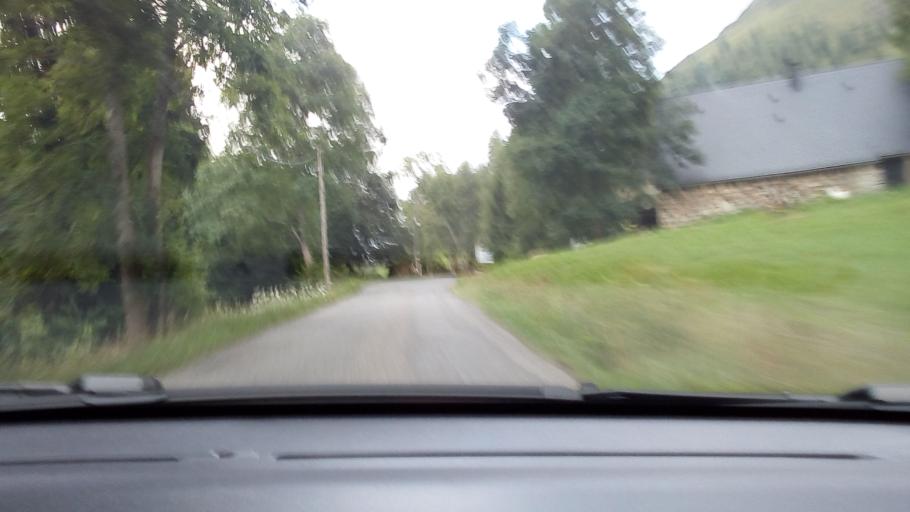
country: FR
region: Midi-Pyrenees
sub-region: Departement des Hautes-Pyrenees
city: Cauterets
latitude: 42.9445
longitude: -0.1833
